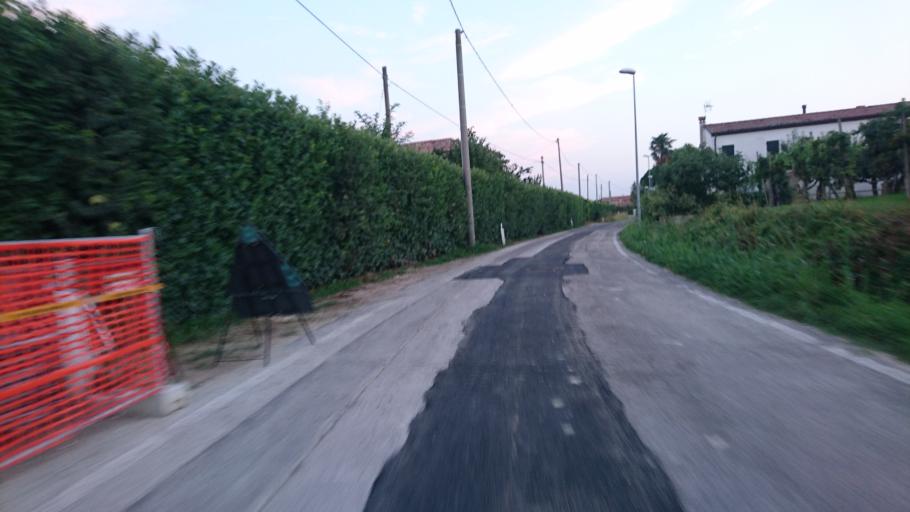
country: IT
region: Veneto
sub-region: Provincia di Padova
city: Tencarola
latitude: 45.3803
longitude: 11.8057
